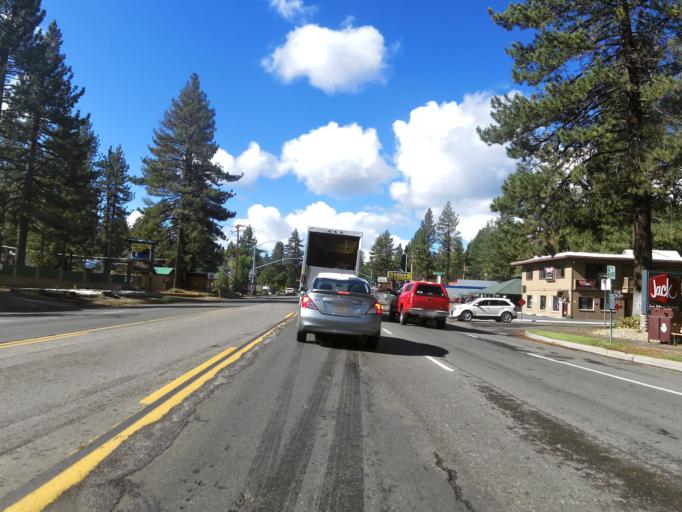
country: US
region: California
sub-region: El Dorado County
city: South Lake Tahoe
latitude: 38.9278
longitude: -119.9827
